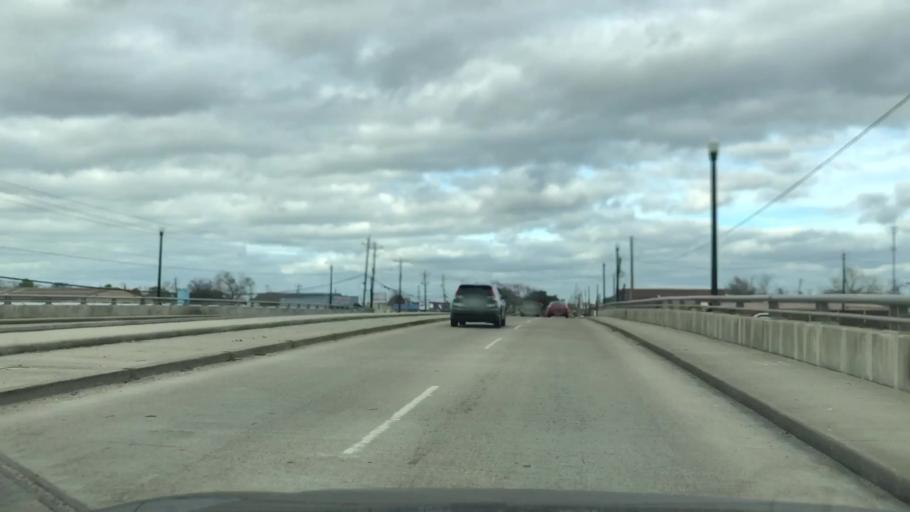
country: US
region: Texas
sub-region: Fort Bend County
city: Missouri City
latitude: 29.6194
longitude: -95.4649
